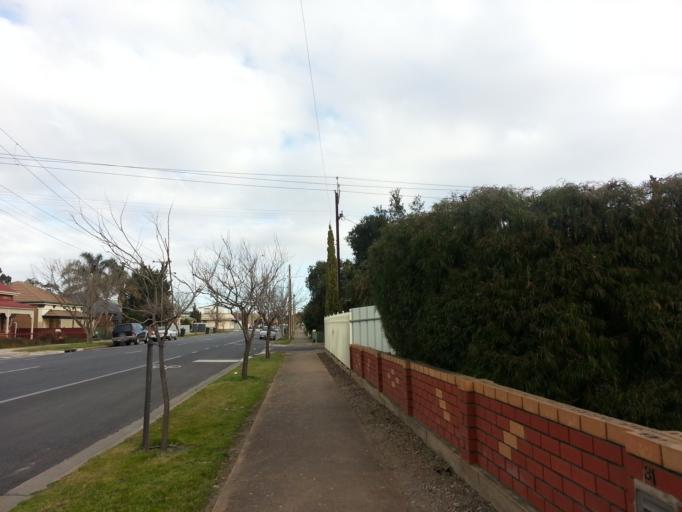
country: AU
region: South Australia
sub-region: Port Adelaide Enfield
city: Alberton
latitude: -34.8487
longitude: 138.5166
